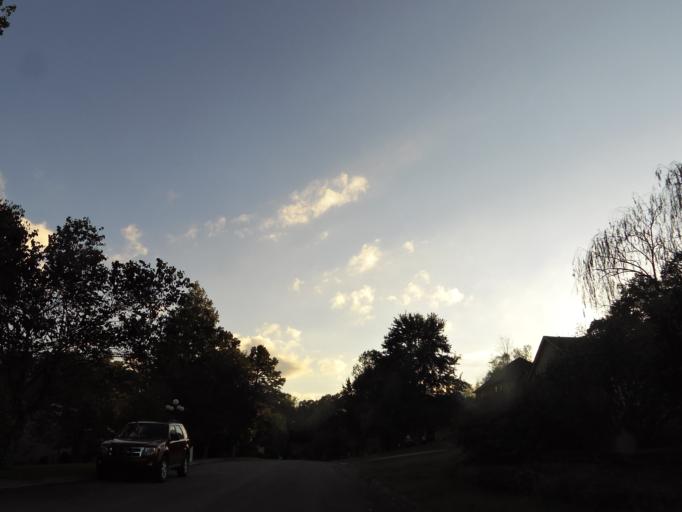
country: US
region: Tennessee
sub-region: Knox County
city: Knoxville
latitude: 35.9050
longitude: -83.9454
